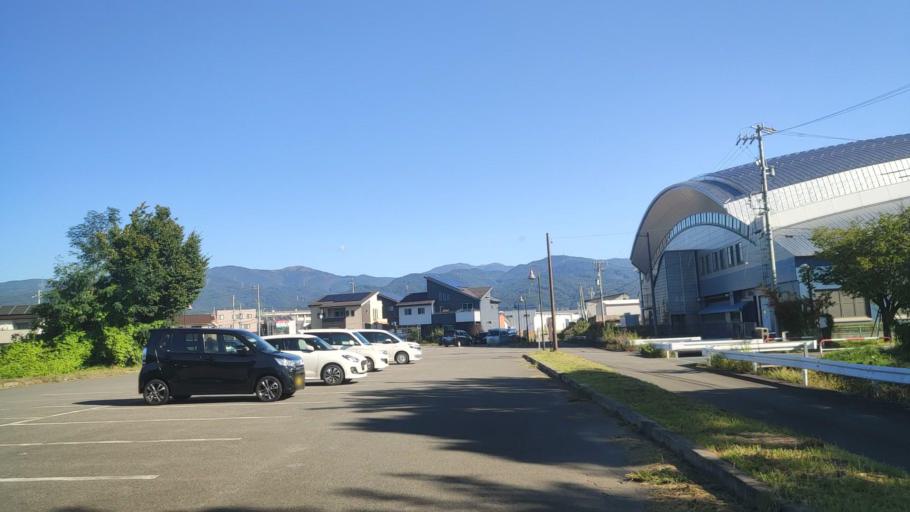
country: JP
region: Nagano
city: Okaya
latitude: 36.0584
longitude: 138.0652
